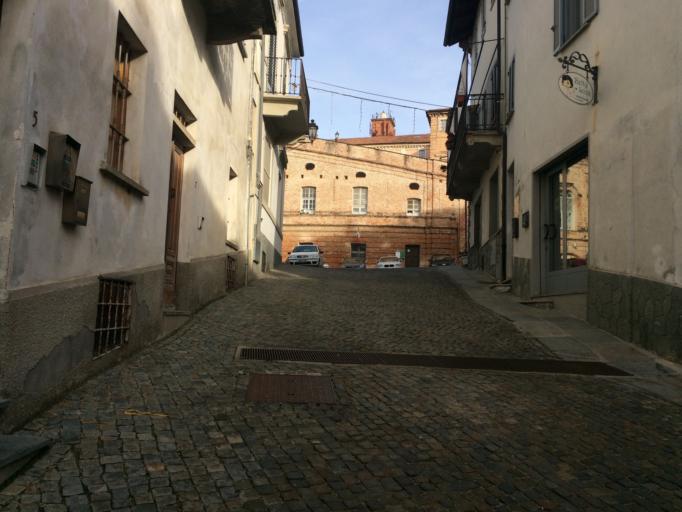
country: IT
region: Piedmont
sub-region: Provincia di Cuneo
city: Govone
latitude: 44.8039
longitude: 8.0999
